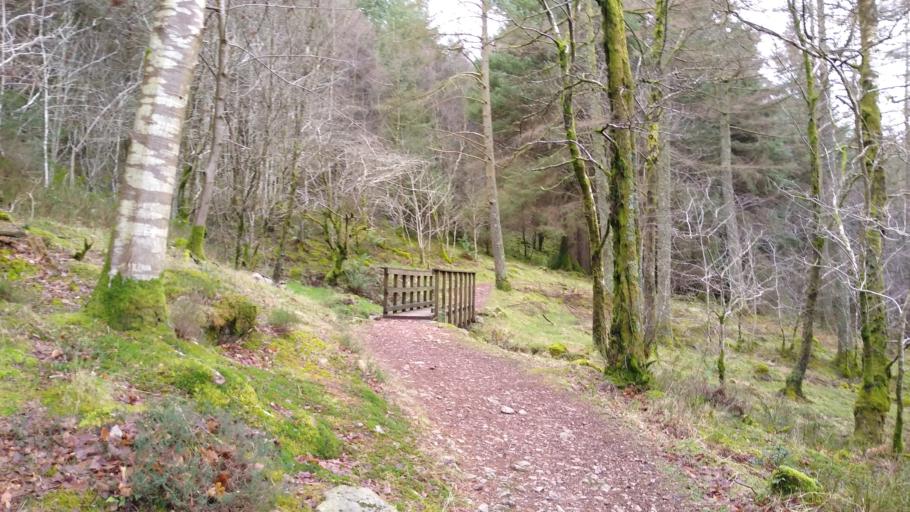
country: GB
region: England
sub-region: Cumbria
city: Frizington
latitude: 54.5223
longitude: -3.3617
